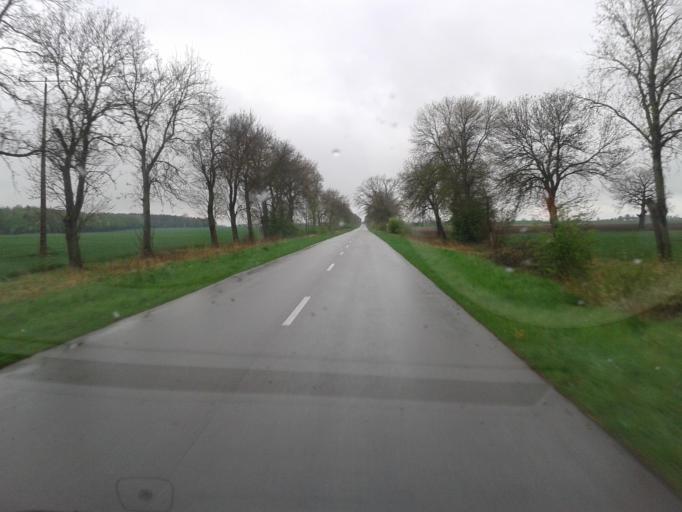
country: UA
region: Lviv
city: Uhniv
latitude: 50.4139
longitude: 23.7403
